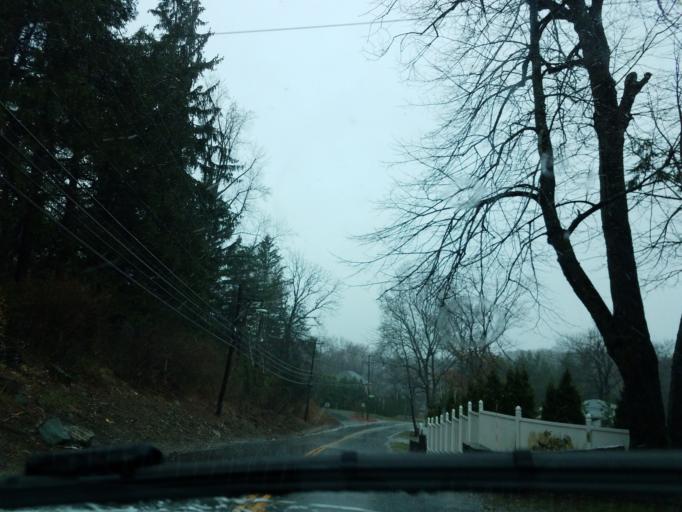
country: US
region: Connecticut
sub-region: New Haven County
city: Waterbury
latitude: 41.5429
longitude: -73.0729
